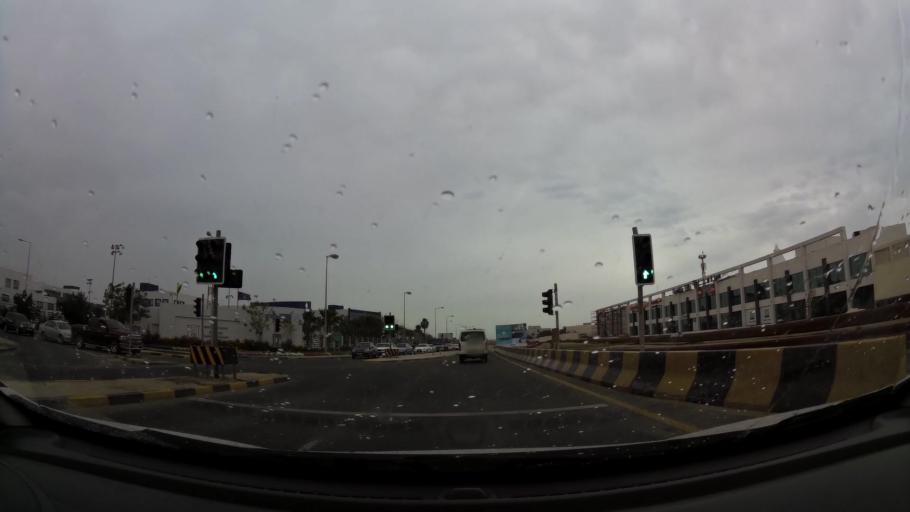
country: BH
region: Central Governorate
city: Madinat Hamad
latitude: 26.1624
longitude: 50.4730
